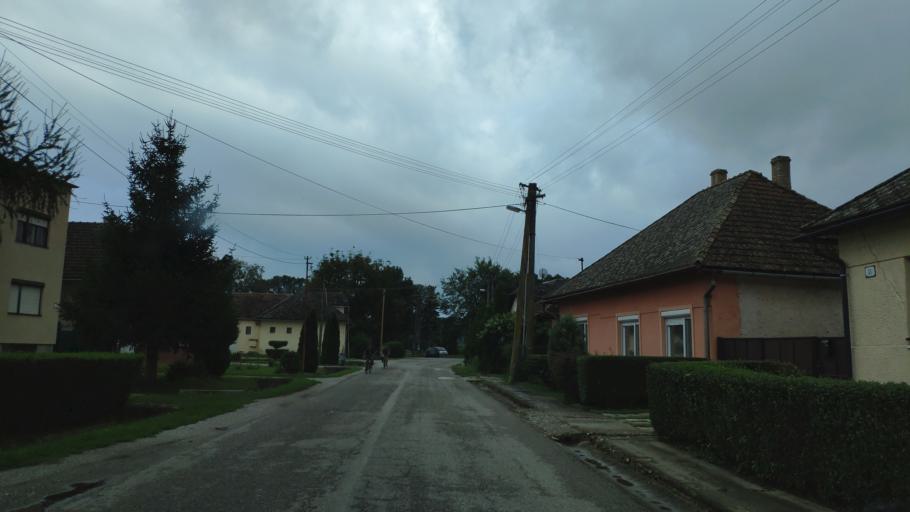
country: SK
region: Kosicky
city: Moldava nad Bodvou
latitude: 48.5773
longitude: 20.8873
